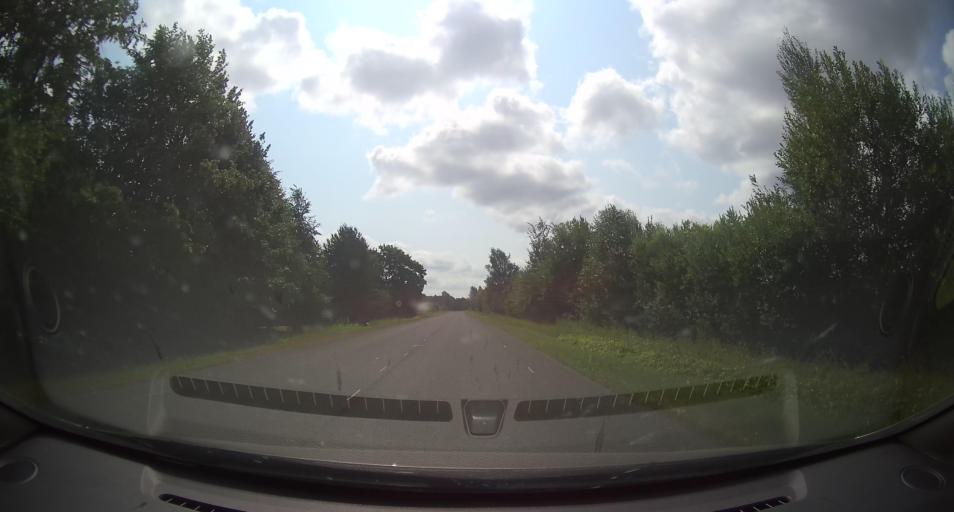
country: EE
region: Paernumaa
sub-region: Audru vald
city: Audru
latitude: 58.4918
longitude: 24.3357
